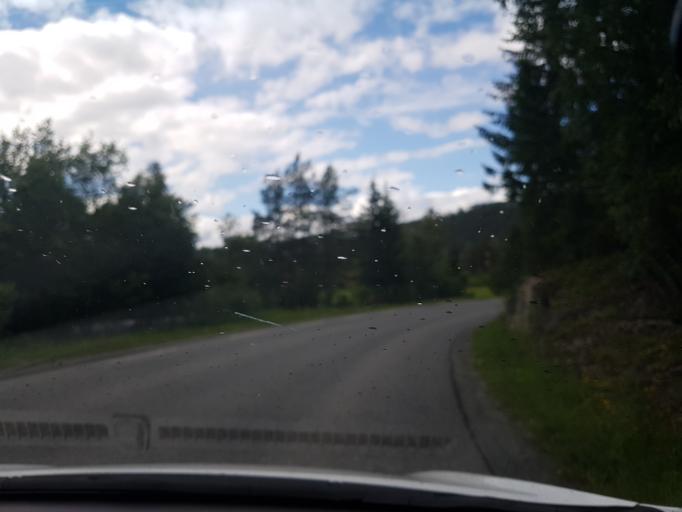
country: NO
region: Nord-Trondelag
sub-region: Stjordal
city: Stjordalshalsen
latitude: 63.6089
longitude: 10.9374
